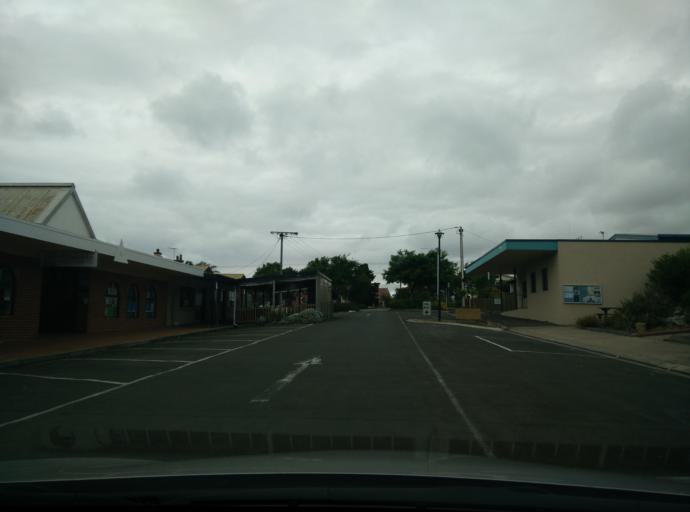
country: AU
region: South Australia
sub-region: Kangaroo Island
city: Kingscote
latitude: -35.6563
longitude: 137.6387
